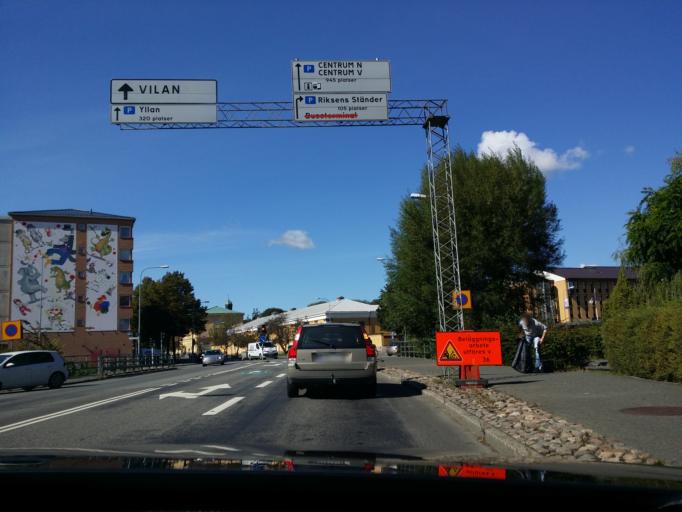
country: SE
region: Skane
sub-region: Kristianstads Kommun
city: Kristianstad
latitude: 56.0268
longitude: 14.1624
